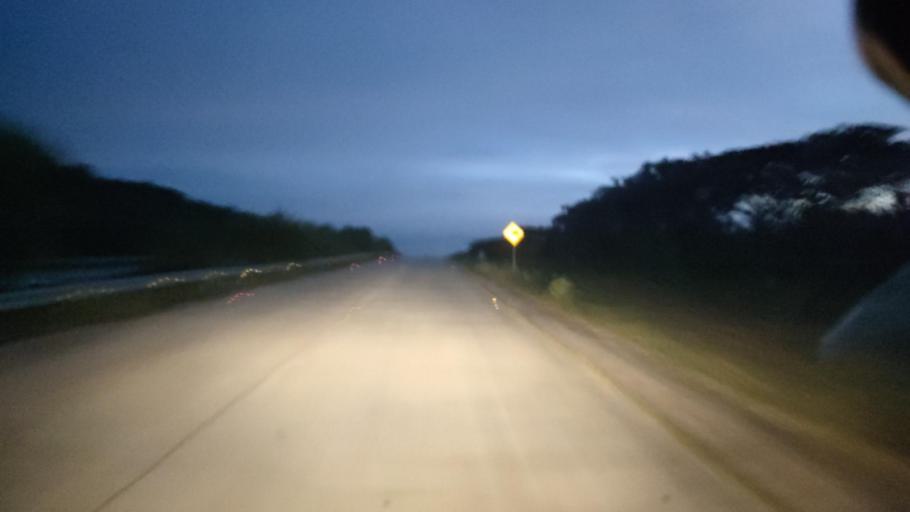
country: MM
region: Mandalay
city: Nay Pyi Taw
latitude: 19.9518
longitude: 95.9893
